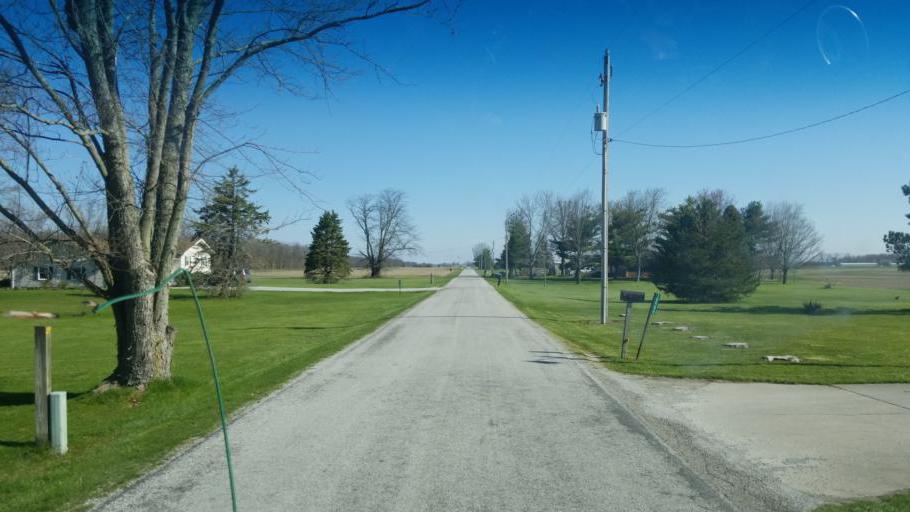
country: US
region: Ohio
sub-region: Hardin County
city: Kenton
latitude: 40.6645
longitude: -83.5621
